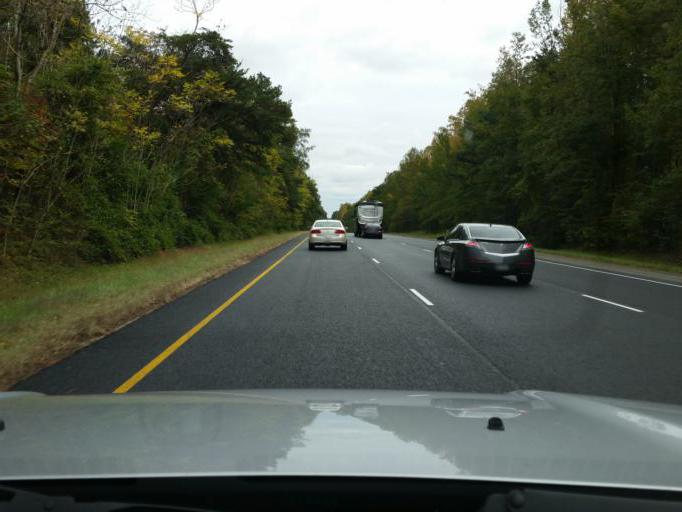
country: US
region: Virginia
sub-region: Henrico County
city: Sandston
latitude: 37.5151
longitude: -77.1834
